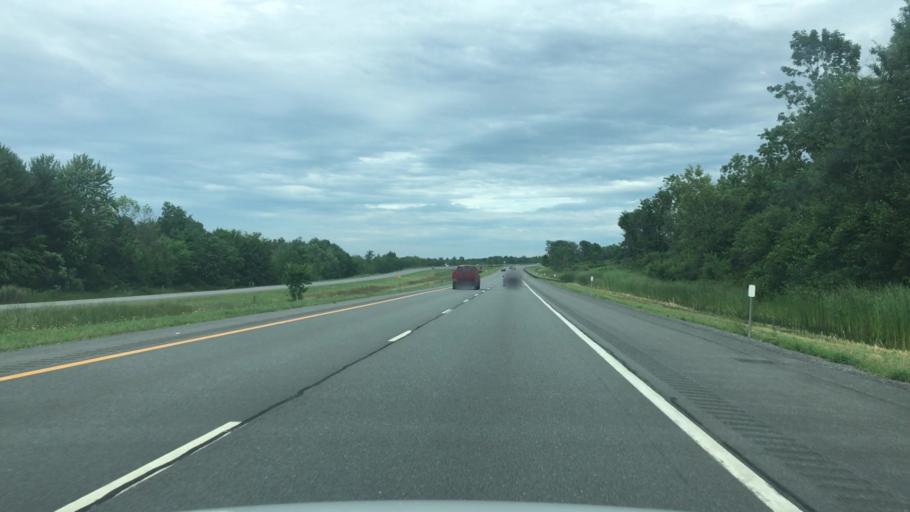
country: US
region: New York
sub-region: Schoharie County
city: Schoharie
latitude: 42.7199
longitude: -74.2505
